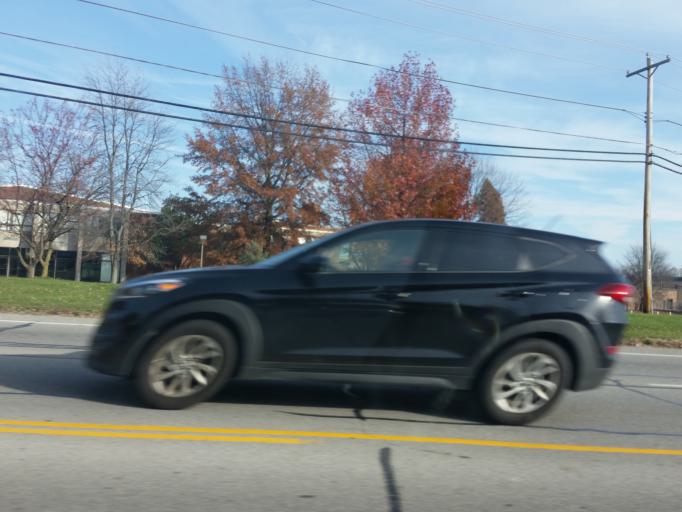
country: US
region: Kentucky
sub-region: Campbell County
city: Alexandria
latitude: 38.9652
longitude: -84.3929
